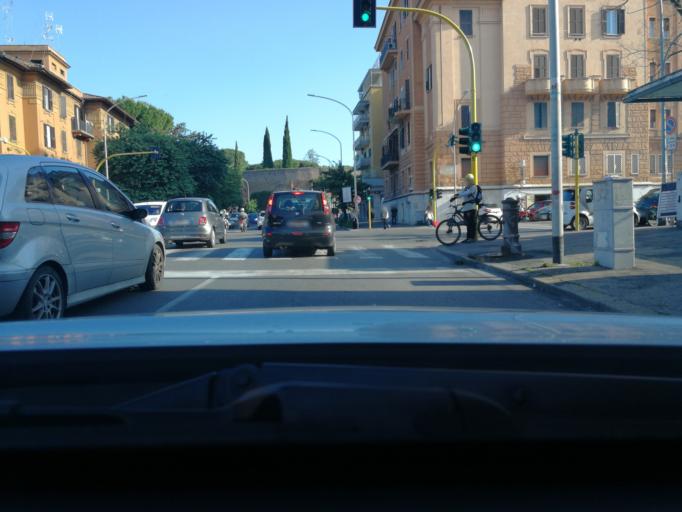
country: IT
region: Latium
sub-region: Citta metropolitana di Roma Capitale
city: Rome
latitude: 41.8860
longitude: 12.5154
